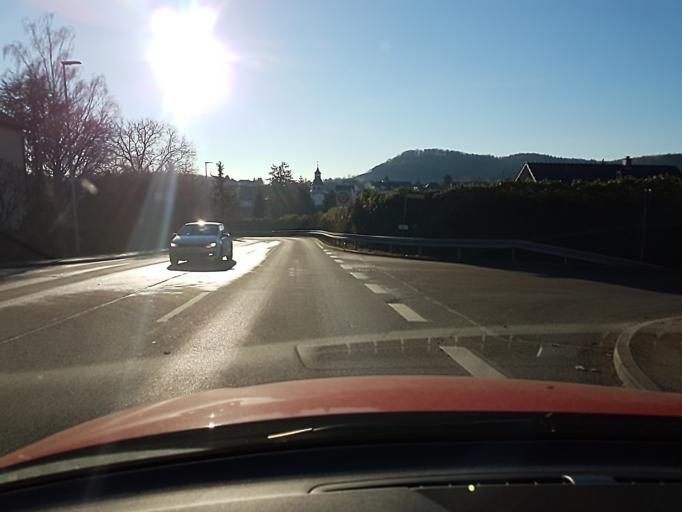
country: DE
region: Baden-Wuerttemberg
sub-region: Regierungsbezirk Stuttgart
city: Freudental
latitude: 49.0118
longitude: 9.0631
